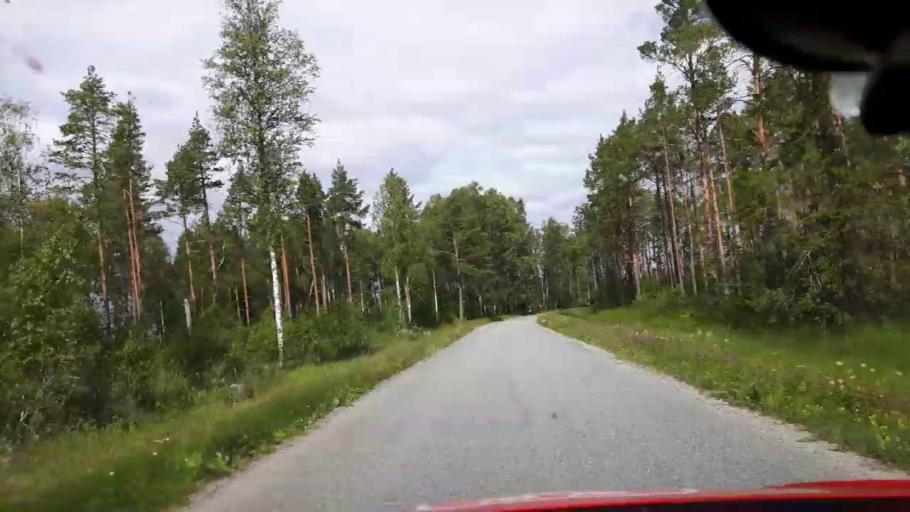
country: SE
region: Jaemtland
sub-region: Braecke Kommun
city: Braecke
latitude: 62.8442
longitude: 15.2969
